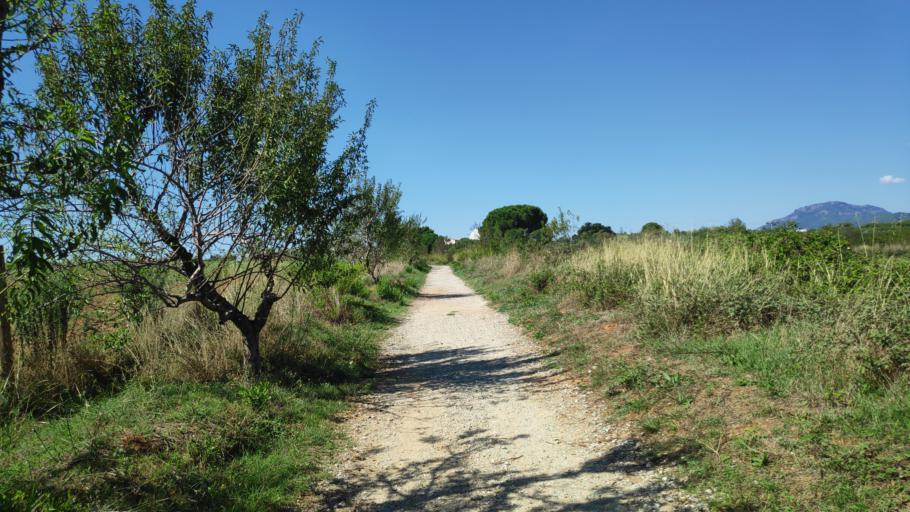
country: ES
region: Catalonia
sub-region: Provincia de Barcelona
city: Sant Quirze del Valles
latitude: 41.5460
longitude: 2.0735
